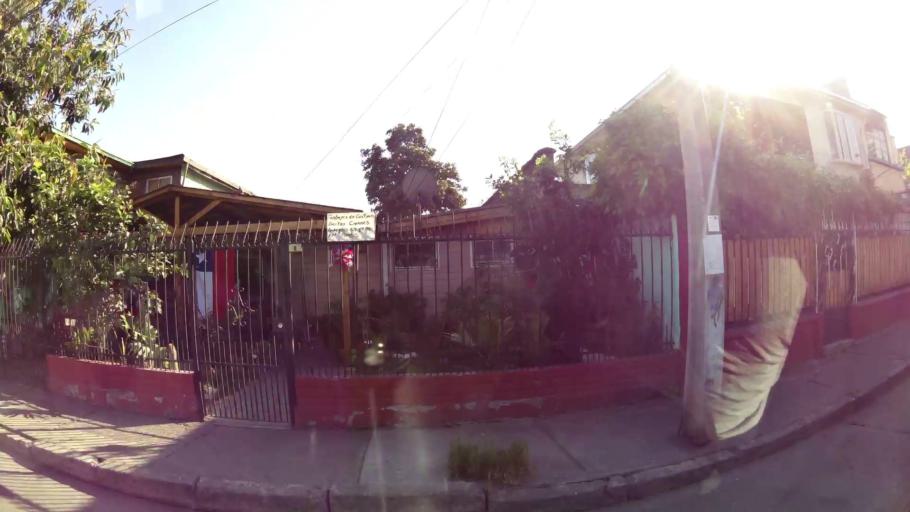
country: CL
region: Santiago Metropolitan
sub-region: Provincia de Santiago
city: Santiago
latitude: -33.3955
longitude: -70.6695
